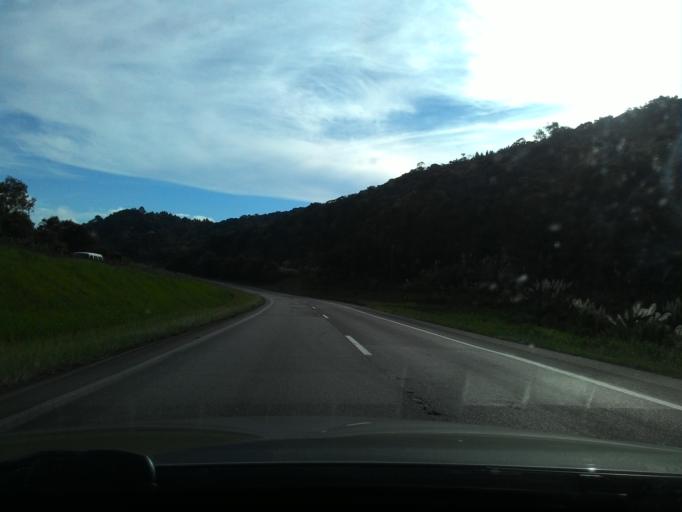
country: BR
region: Parana
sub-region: Campina Grande Do Sul
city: Campina Grande do Sul
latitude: -25.2483
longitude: -48.9071
